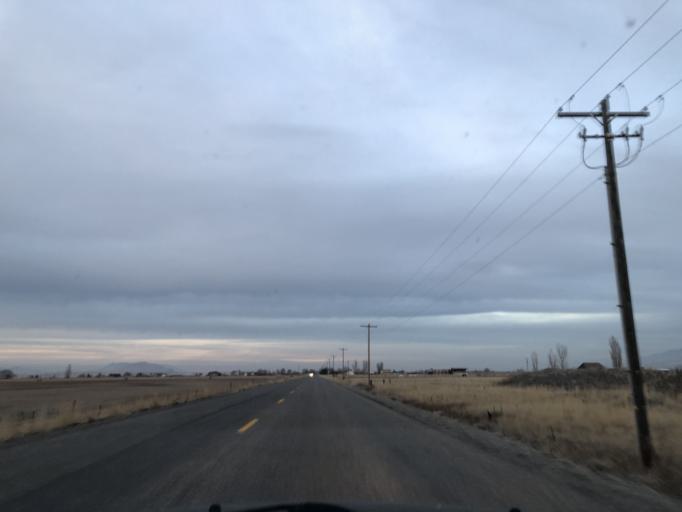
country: US
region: Utah
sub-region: Cache County
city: Benson
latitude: 41.7712
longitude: -111.9117
